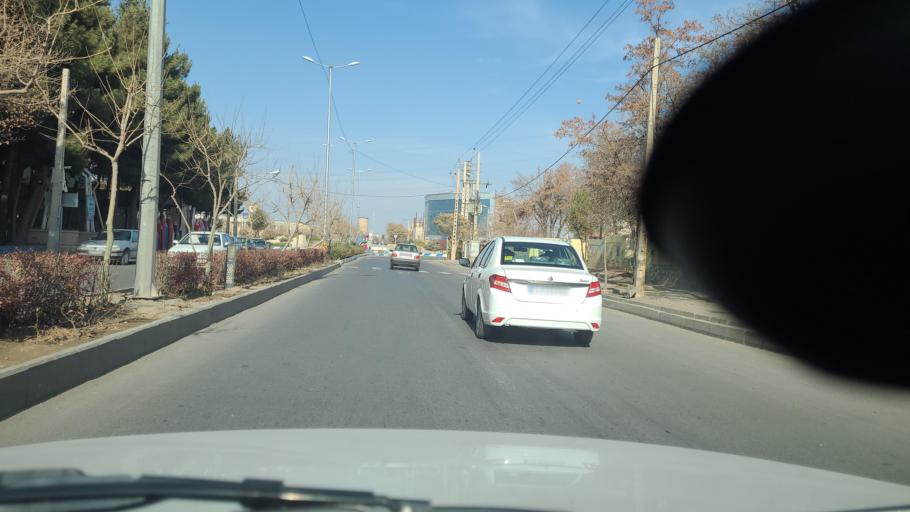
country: IR
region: Razavi Khorasan
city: Fariman
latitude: 35.6932
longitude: 59.8442
